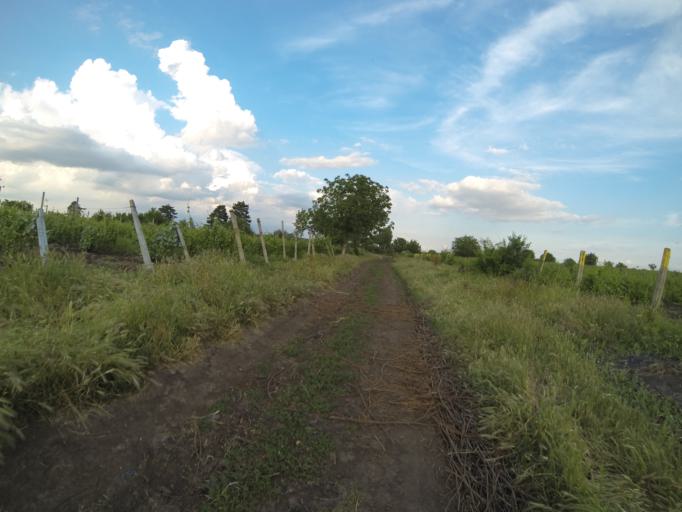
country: RO
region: Dolj
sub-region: Comuna Ceratu
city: Ceratu
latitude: 44.1138
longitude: 23.6815
